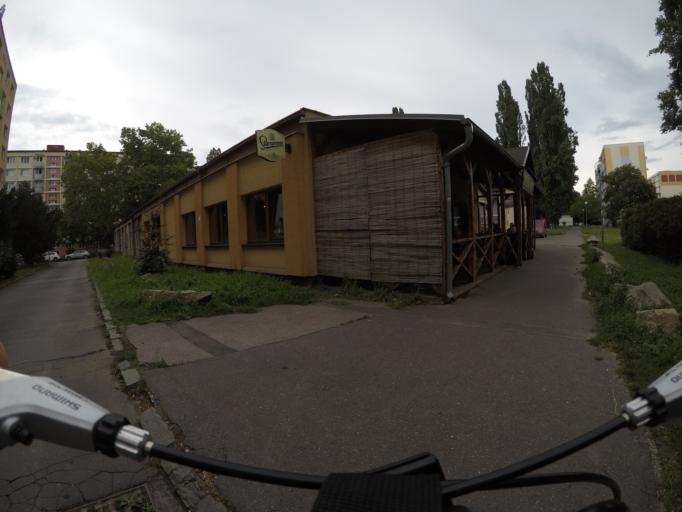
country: SK
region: Bratislavsky
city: Bratislava
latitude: 48.1555
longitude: 17.1701
